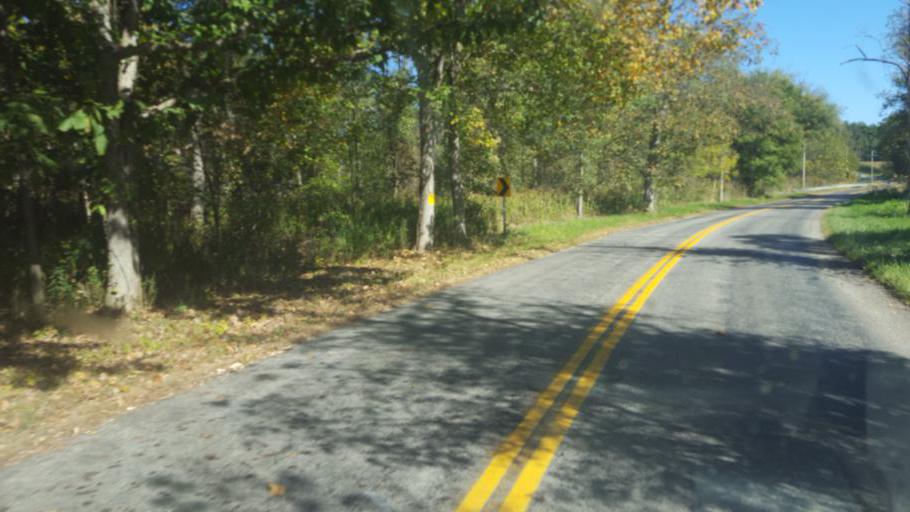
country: US
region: Ohio
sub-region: Huron County
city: New London
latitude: 40.9932
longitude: -82.3987
